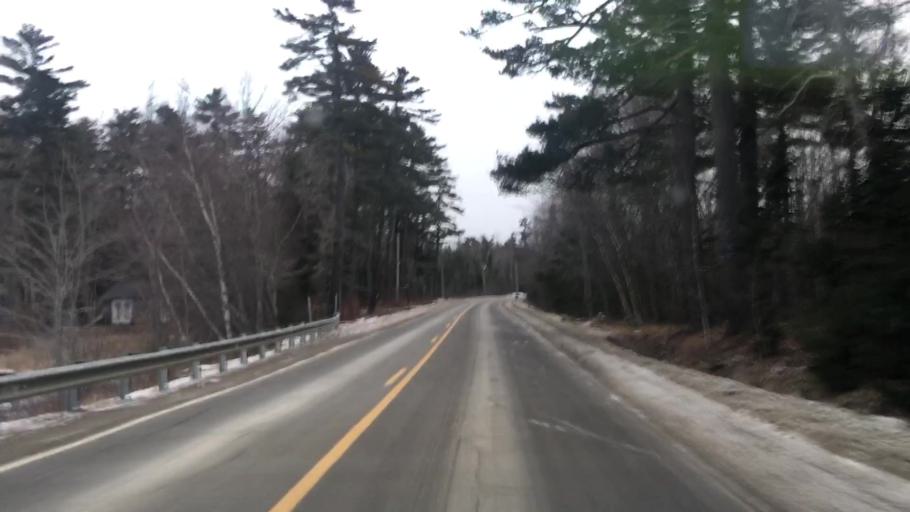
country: US
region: Maine
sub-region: Hancock County
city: Ellsworth
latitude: 44.6159
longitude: -68.3857
